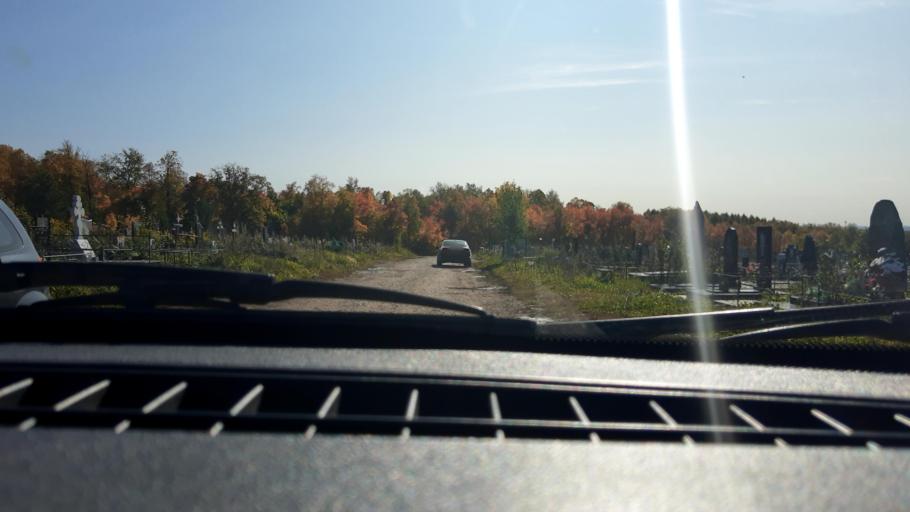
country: RU
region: Bashkortostan
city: Mikhaylovka
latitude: 54.8145
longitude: 55.8616
